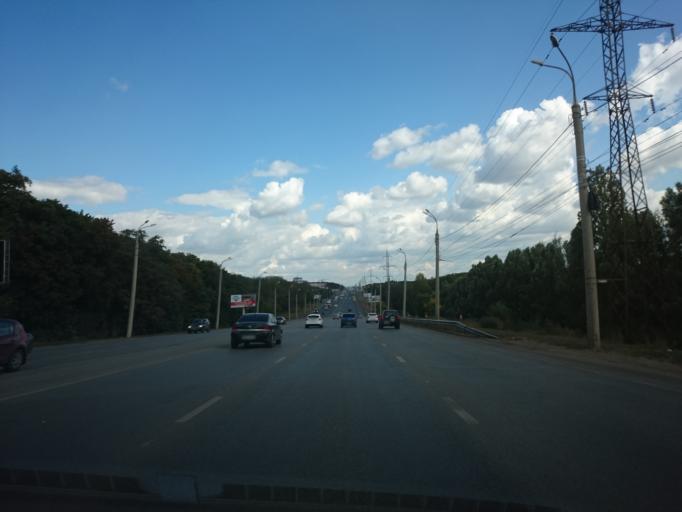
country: RU
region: Samara
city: Samara
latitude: 53.2657
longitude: 50.2478
